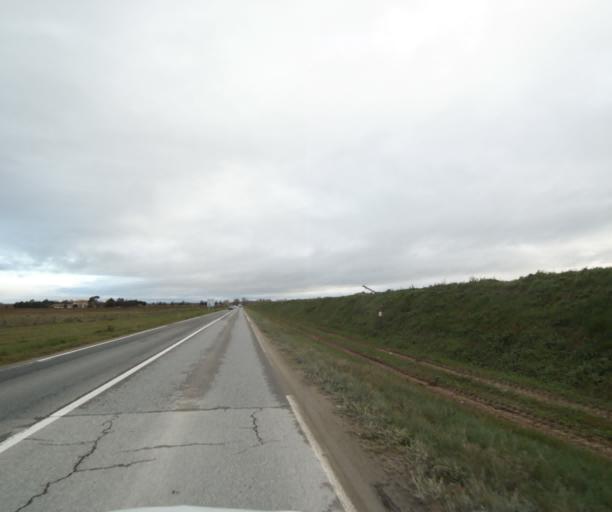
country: FR
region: Midi-Pyrenees
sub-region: Departement de l'Ariege
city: Saverdun
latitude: 43.2045
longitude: 1.6090
